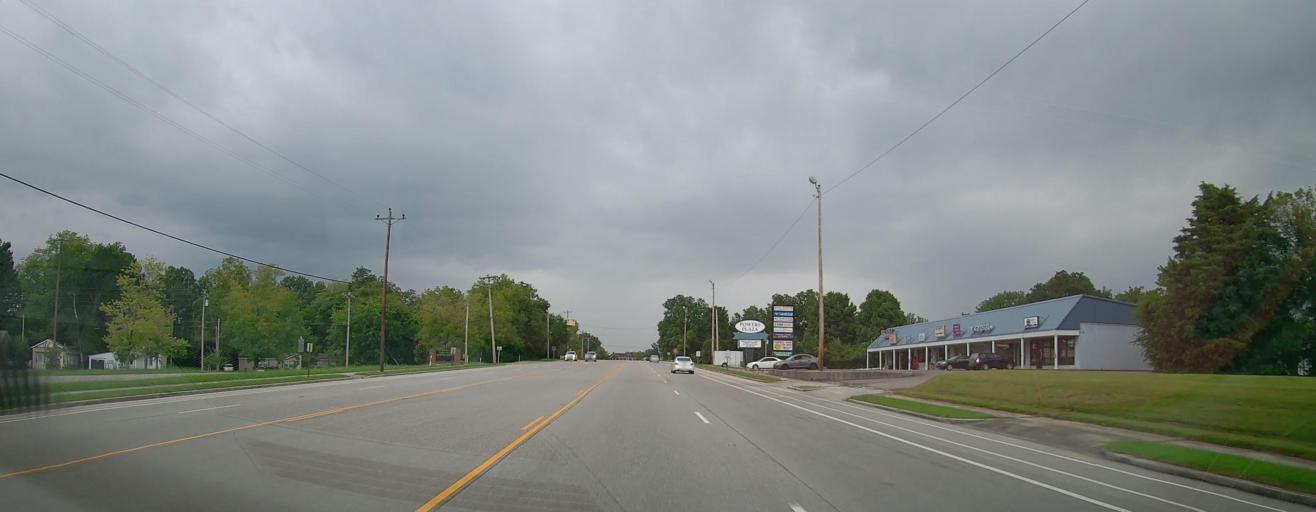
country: US
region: Tennessee
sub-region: Coffee County
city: Manchester
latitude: 35.4787
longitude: -86.0838
